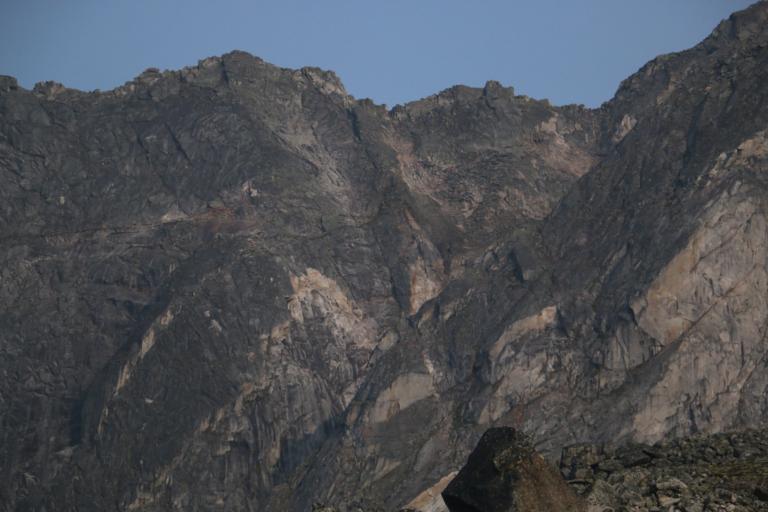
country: RU
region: Respublika Buryatiya
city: Novyy Uoyan
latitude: 56.2220
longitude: 110.9878
